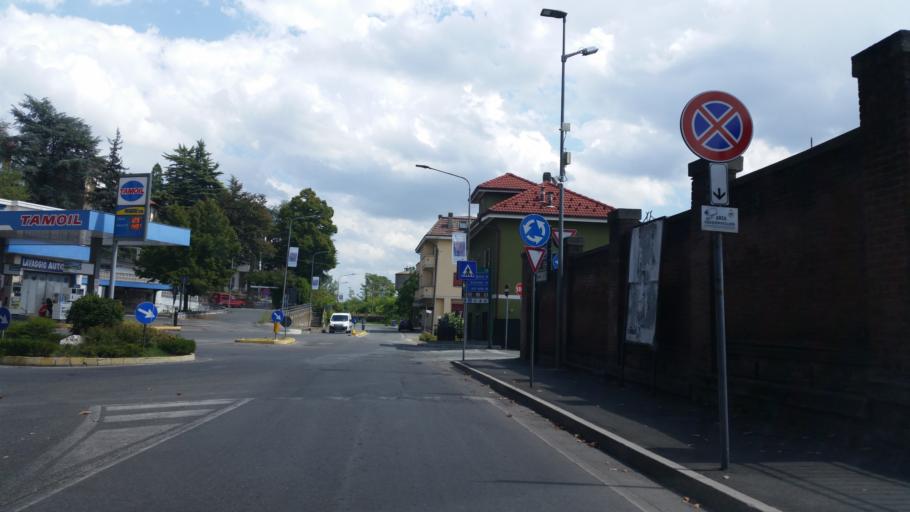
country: IT
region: Piedmont
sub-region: Provincia di Alessandria
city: Acqui Terme
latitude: 44.6730
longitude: 8.4767
